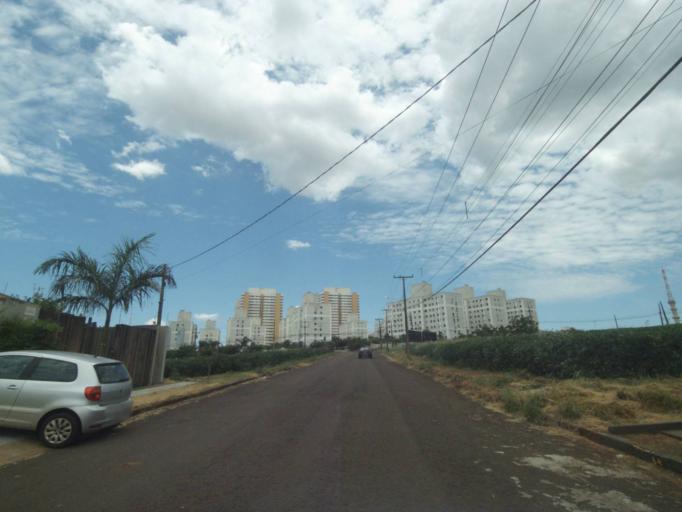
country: BR
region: Parana
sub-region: Londrina
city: Londrina
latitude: -23.3218
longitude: -51.1951
